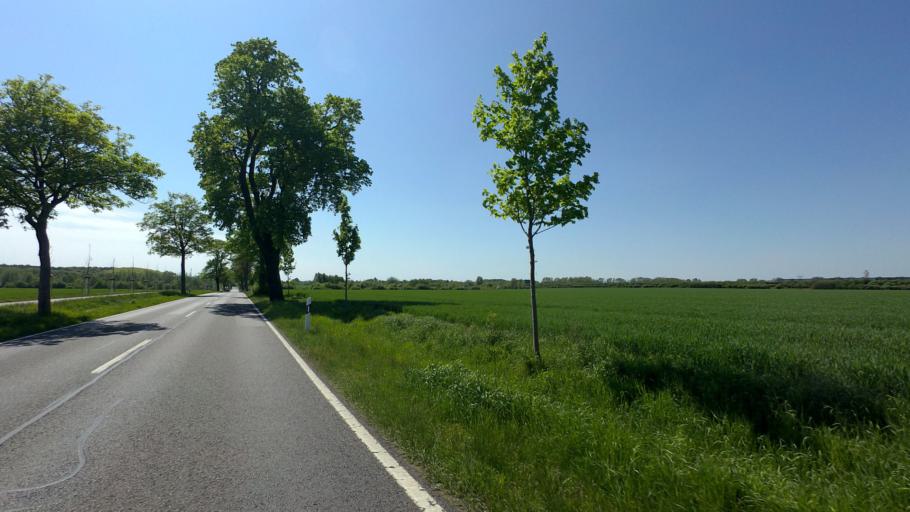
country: DE
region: Brandenburg
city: Schulzendorf
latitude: 52.3548
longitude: 13.5575
